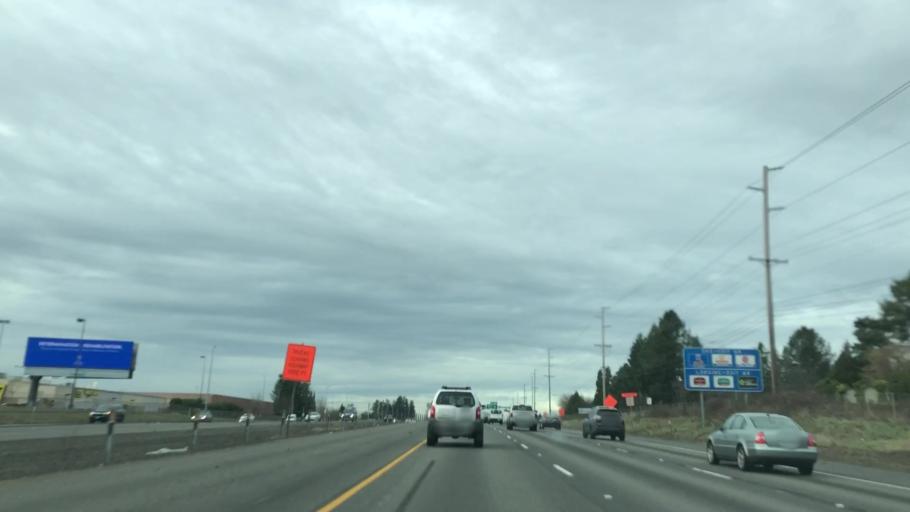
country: US
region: Oregon
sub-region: Washington County
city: Oak Hills
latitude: 45.5392
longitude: -122.8598
